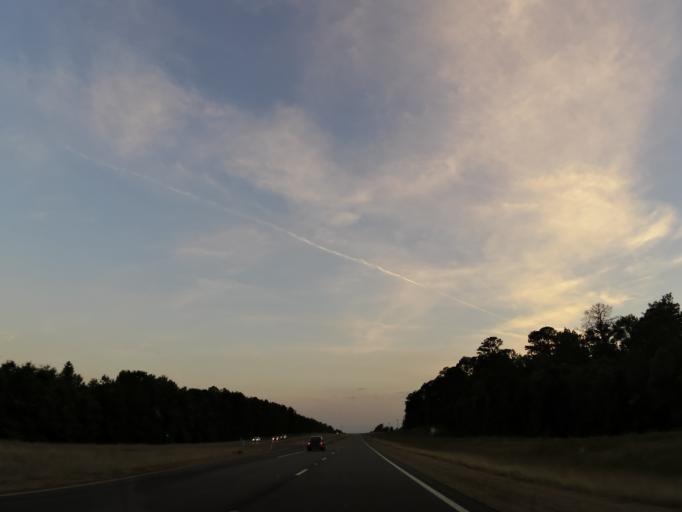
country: US
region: Mississippi
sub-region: Kemper County
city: De Kalb
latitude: 32.7969
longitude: -88.4560
